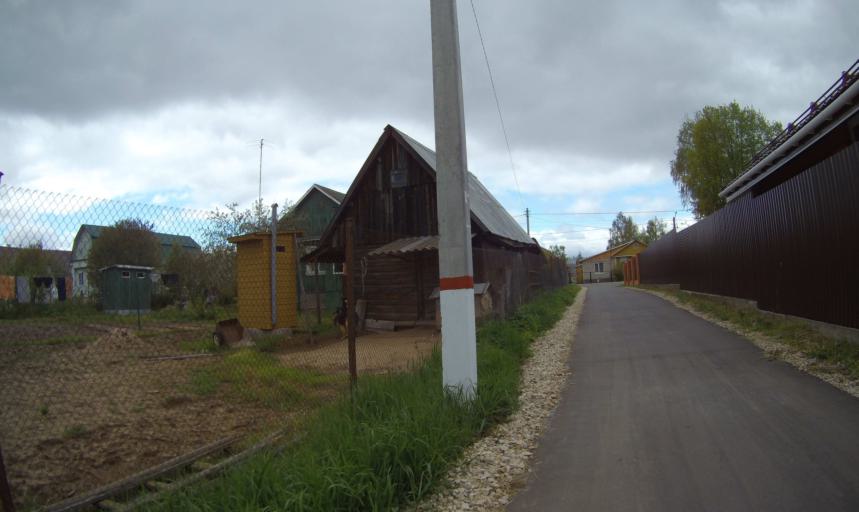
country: RU
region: Moskovskaya
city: Rechitsy
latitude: 55.5402
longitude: 38.4301
